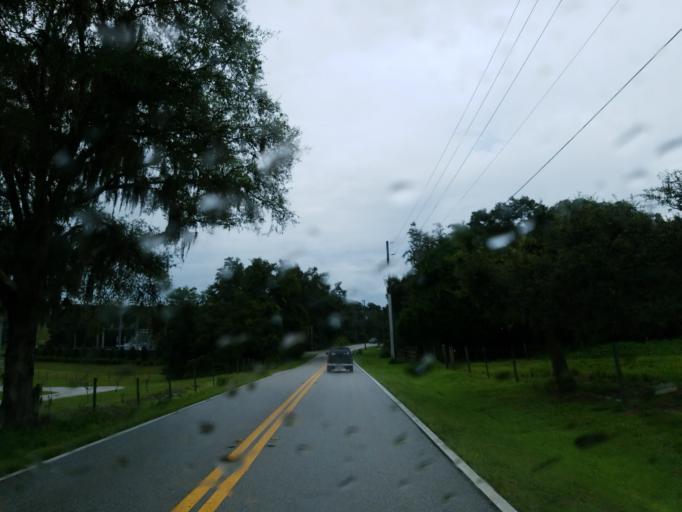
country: US
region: Florida
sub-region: Hernando County
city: Brooksville
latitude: 28.5843
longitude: -82.3435
